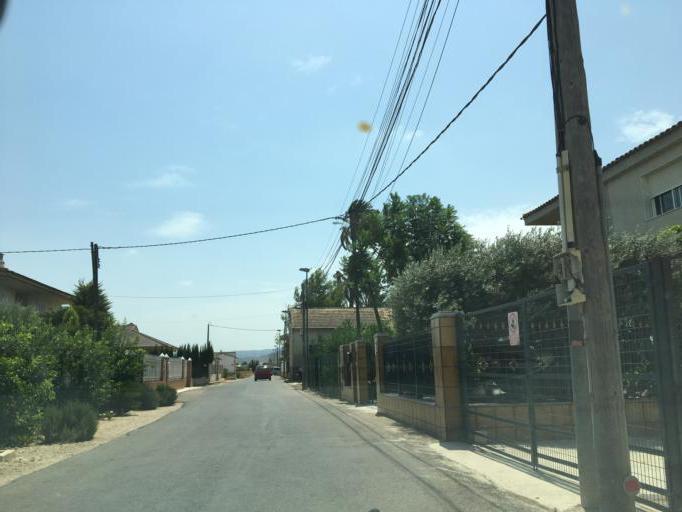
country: ES
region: Murcia
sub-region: Murcia
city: Santomera
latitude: 38.0333
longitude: -1.0526
